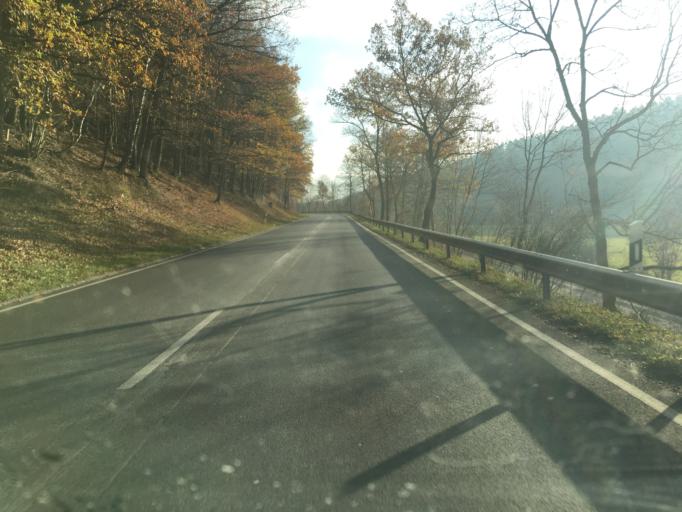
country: DE
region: North Rhine-Westphalia
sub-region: Regierungsbezirk Koln
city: Kall
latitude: 50.5638
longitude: 6.5332
